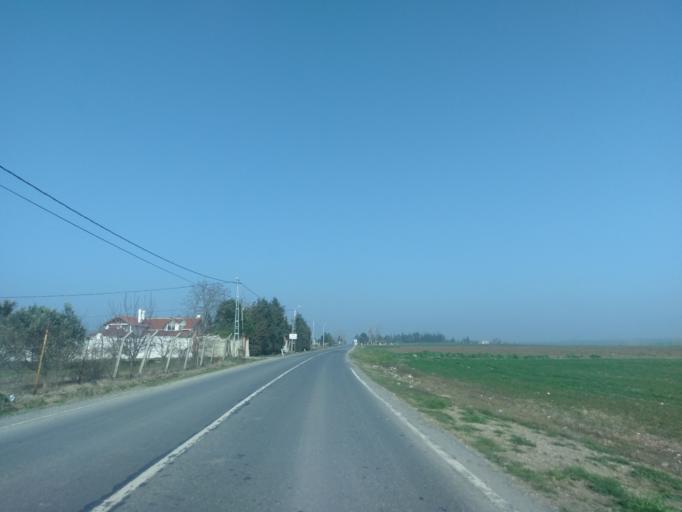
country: TR
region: Istanbul
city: Silivri
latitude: 41.0904
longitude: 28.2715
